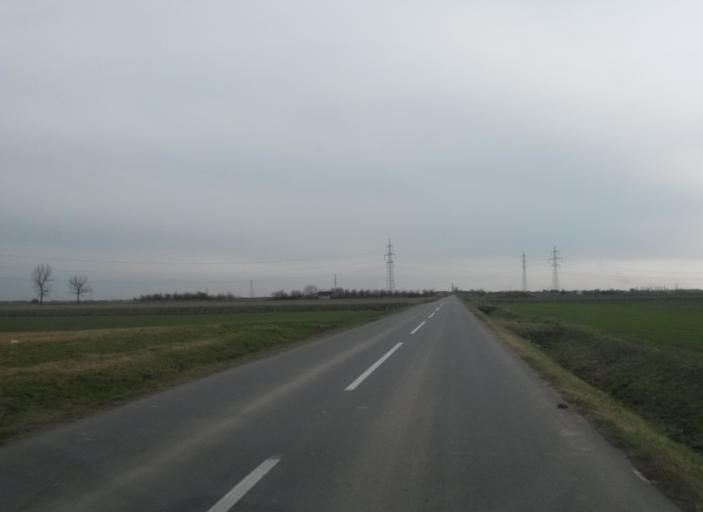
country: HR
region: Osjecko-Baranjska
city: Ovcara
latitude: 45.4965
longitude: 18.6172
